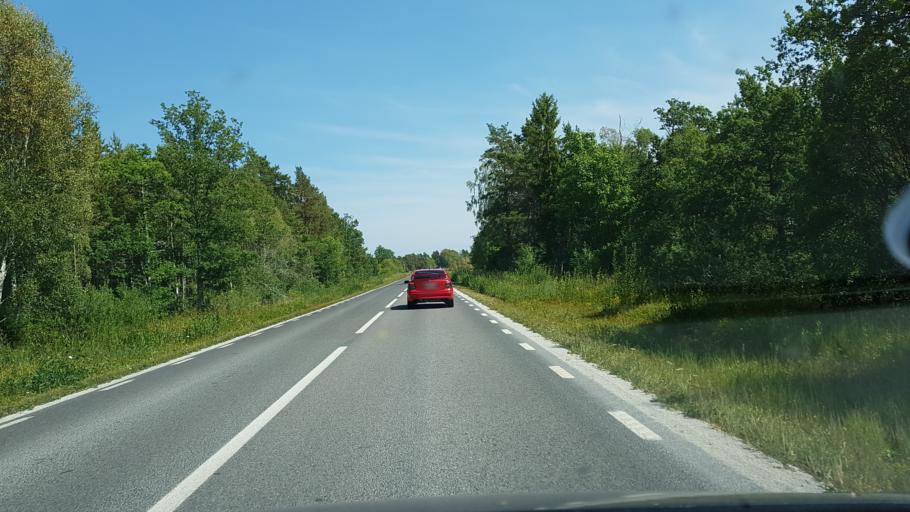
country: SE
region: Gotland
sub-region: Gotland
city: Visby
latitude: 57.6397
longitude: 18.4981
